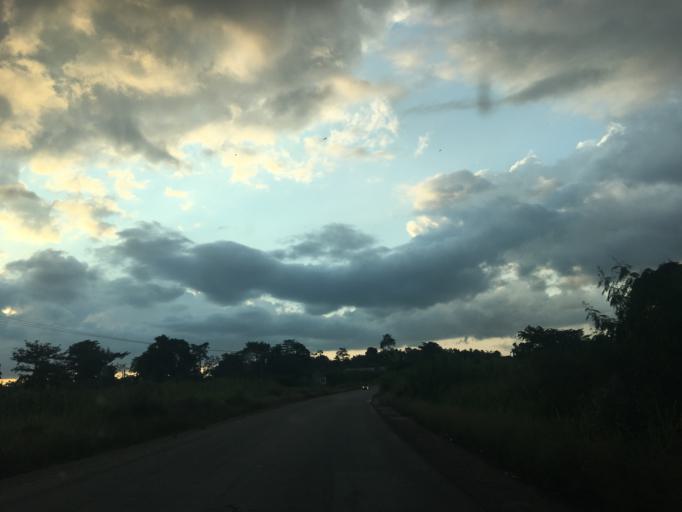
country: GH
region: Western
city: Bibiani
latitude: 6.7659
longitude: -2.5084
